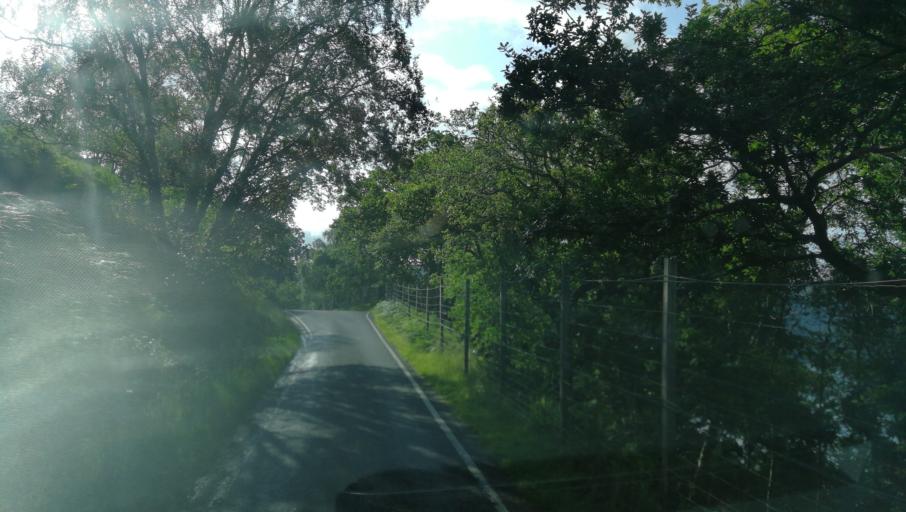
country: GB
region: Scotland
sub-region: Argyll and Bute
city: Isle Of Mull
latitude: 56.6817
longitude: -5.8607
